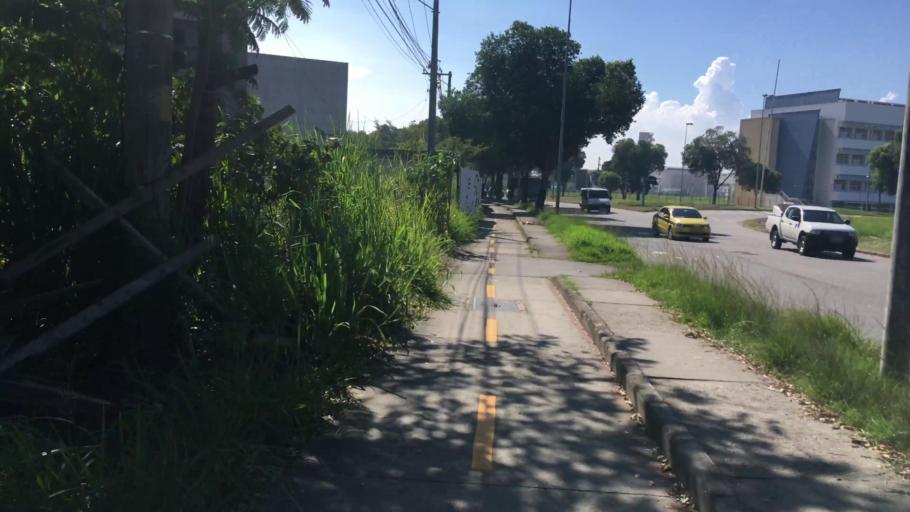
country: BR
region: Rio de Janeiro
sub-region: Rio De Janeiro
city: Rio de Janeiro
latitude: -22.8571
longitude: -43.2305
